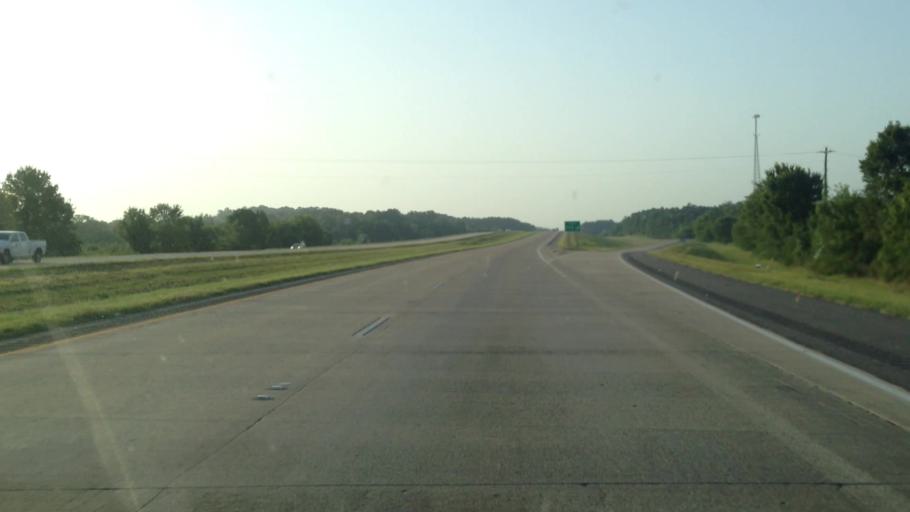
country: US
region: Louisiana
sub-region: Grant Parish
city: Colfax
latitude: 31.4983
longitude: -92.8670
